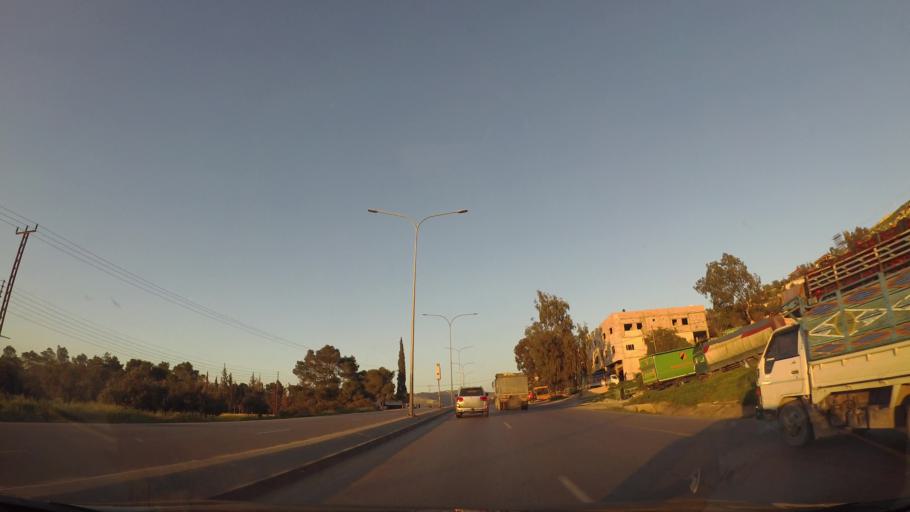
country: JO
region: Amman
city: Umm as Summaq
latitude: 31.8757
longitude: 35.7785
